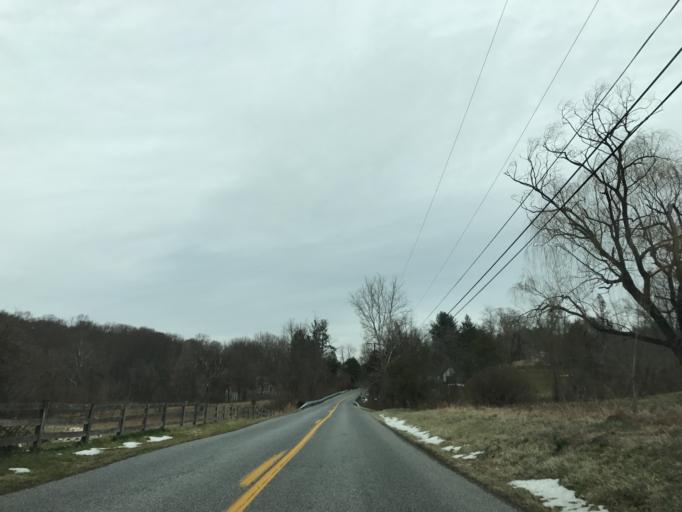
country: US
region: Maryland
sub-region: Baltimore County
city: Hunt Valley
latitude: 39.5549
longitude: -76.7181
